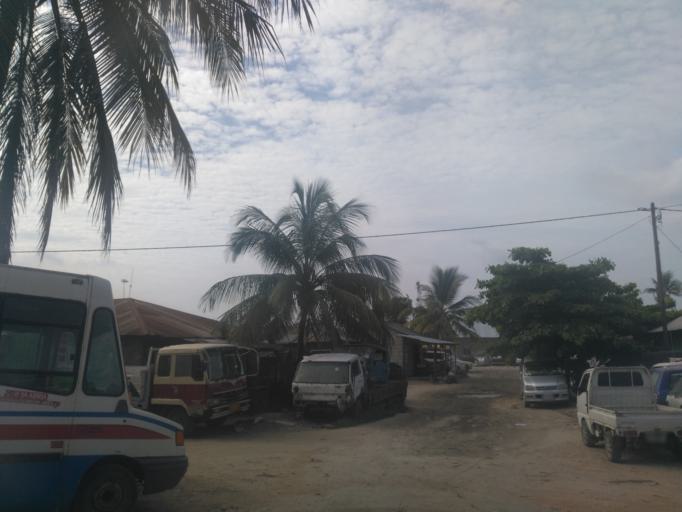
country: TZ
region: Zanzibar Urban/West
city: Zanzibar
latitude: -6.1590
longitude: 39.2070
